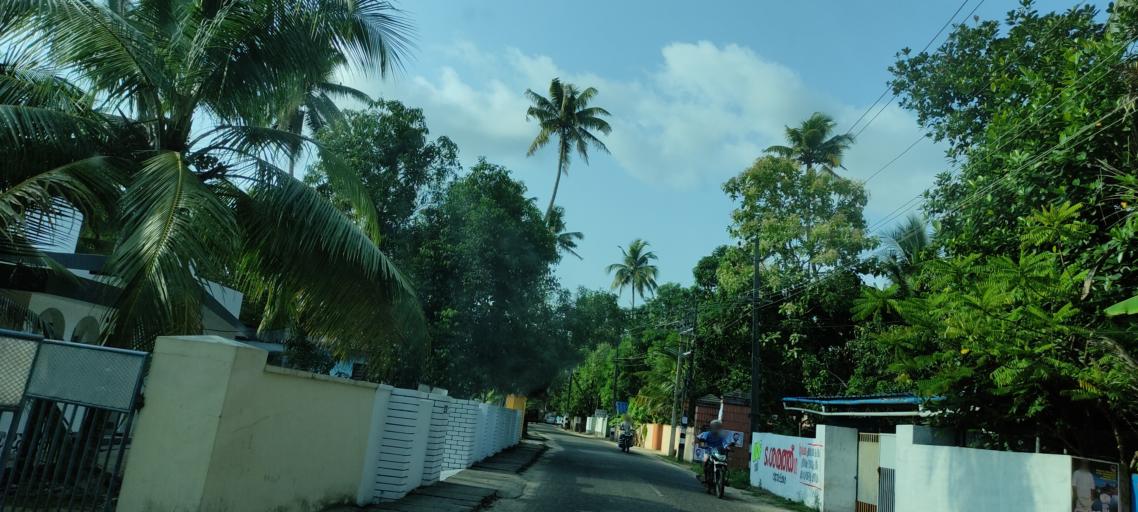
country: IN
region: Kerala
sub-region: Alappuzha
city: Vayalar
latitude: 9.7043
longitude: 76.2892
